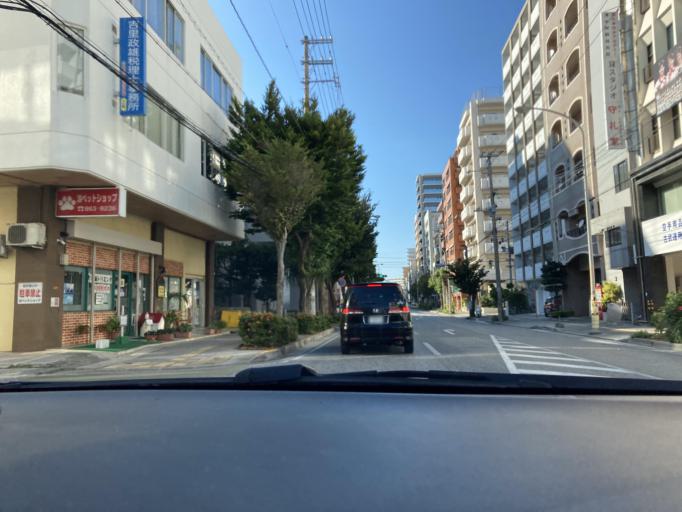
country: JP
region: Okinawa
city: Naha-shi
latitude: 26.2209
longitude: 127.6891
